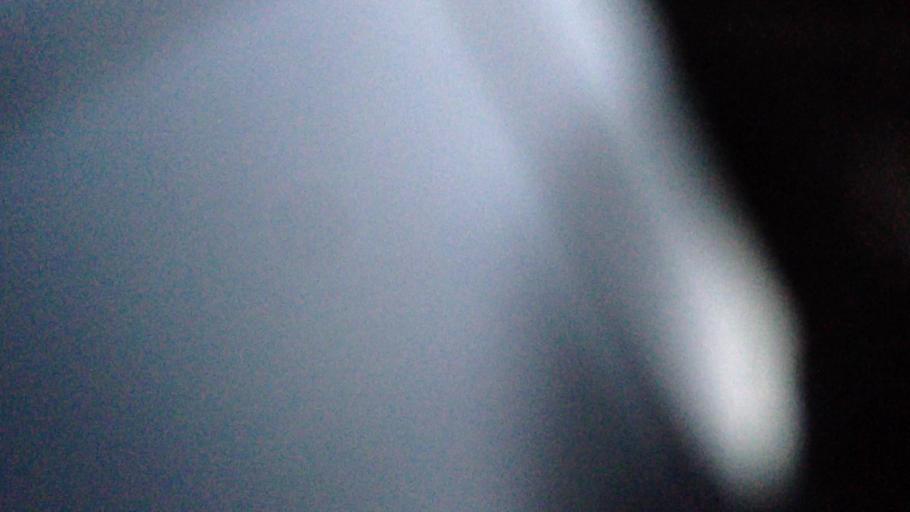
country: US
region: New York
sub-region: Columbia County
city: Lorenz Park
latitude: 42.2730
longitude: -73.7655
